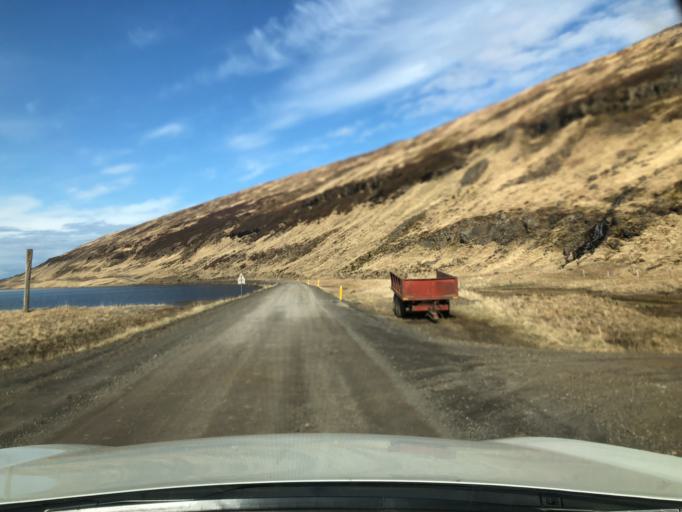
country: IS
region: West
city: Borgarnes
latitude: 65.0591
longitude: -21.5799
